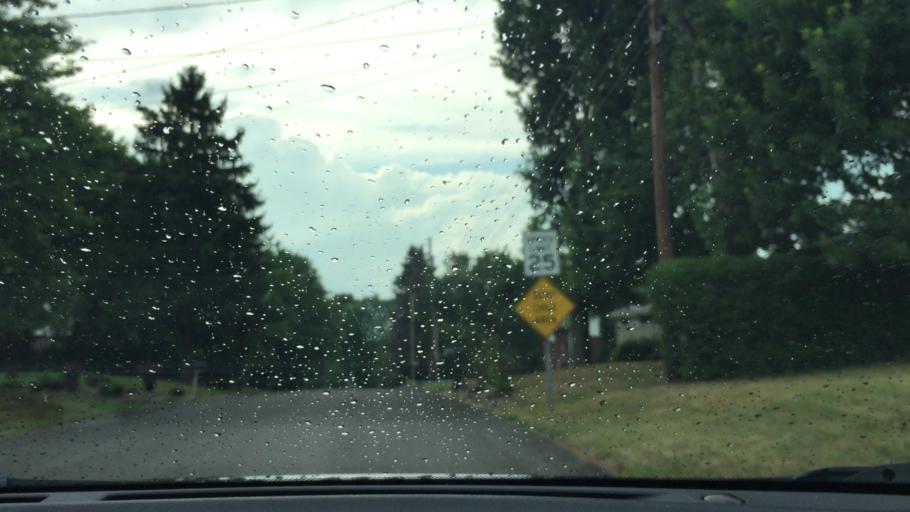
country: US
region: Pennsylvania
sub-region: Butler County
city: Fernway
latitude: 40.6799
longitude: -80.1285
